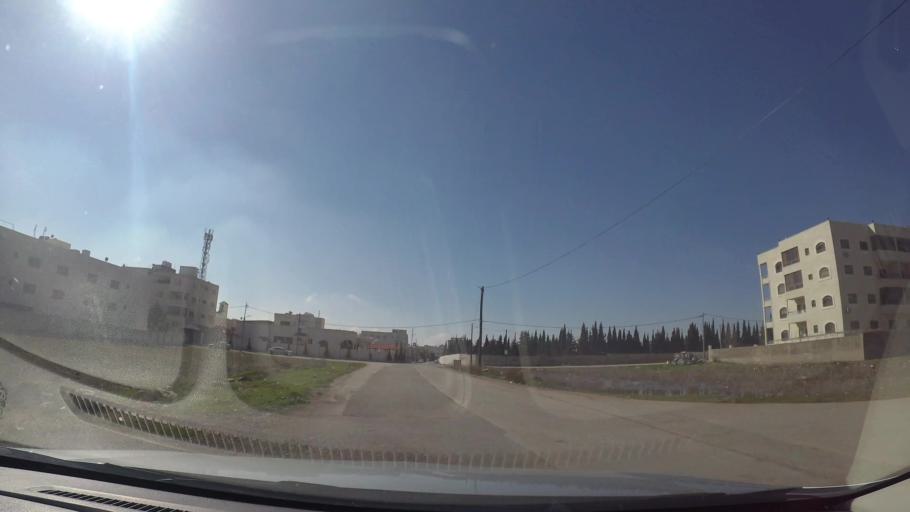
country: JO
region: Amman
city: Al Bunayyat ash Shamaliyah
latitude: 31.9041
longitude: 35.8950
